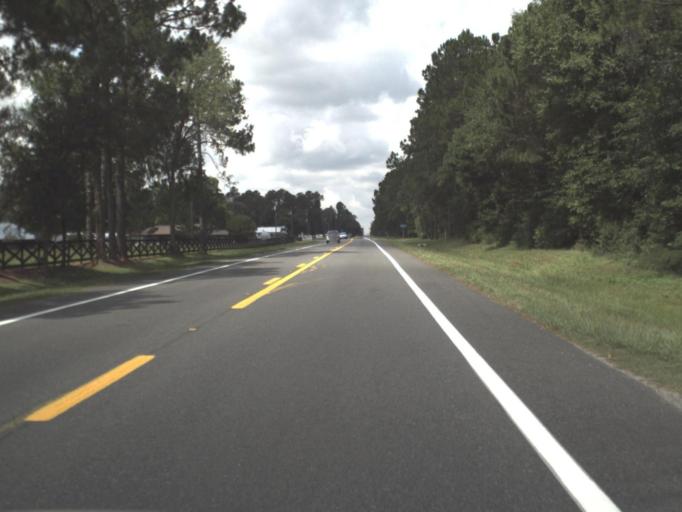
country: US
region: Florida
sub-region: Union County
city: Lake Butler
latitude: 30.0048
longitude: -82.3674
